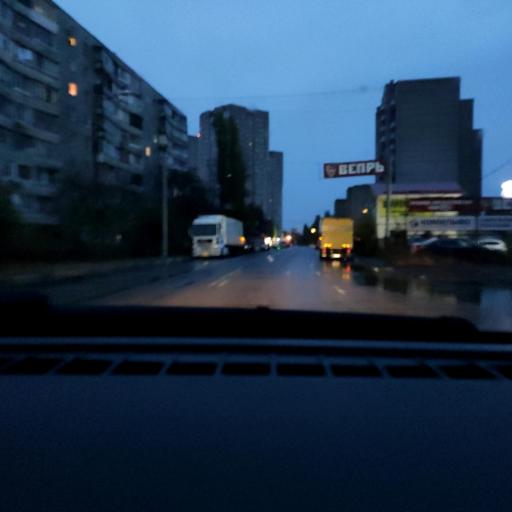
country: RU
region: Voronezj
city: Voronezh
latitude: 51.6793
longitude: 39.2535
